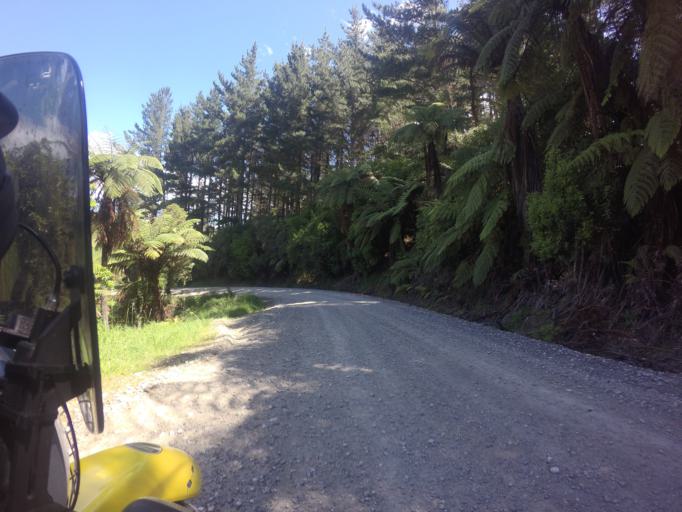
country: NZ
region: Hawke's Bay
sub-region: Wairoa District
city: Wairoa
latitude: -38.9822
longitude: 177.7028
